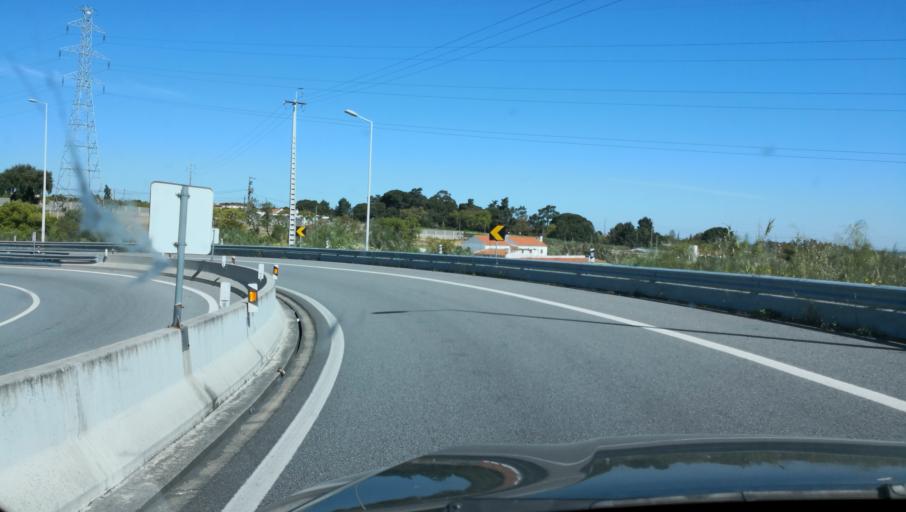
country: PT
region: Setubal
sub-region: Palmela
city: Palmela
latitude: 38.5857
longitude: -8.8855
